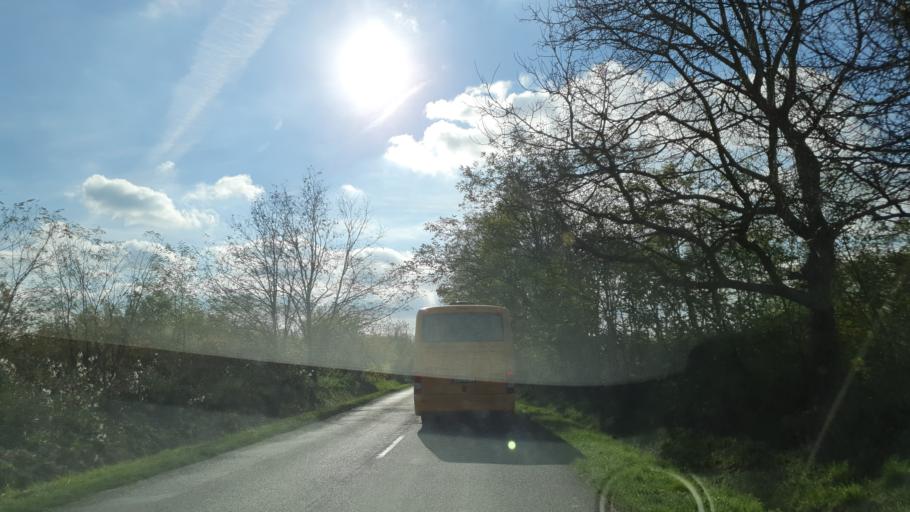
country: HU
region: Szabolcs-Szatmar-Bereg
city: Gyulahaza
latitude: 48.1240
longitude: 22.0884
